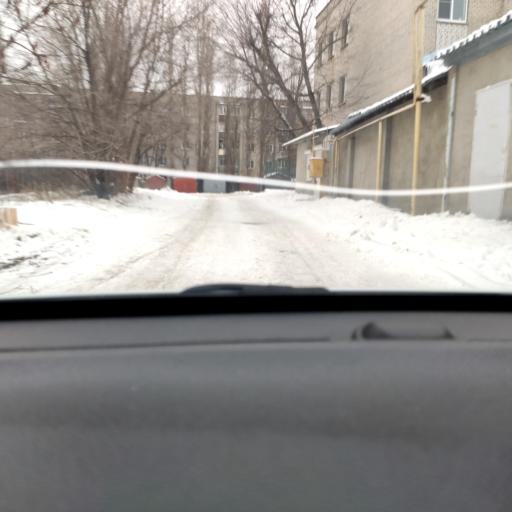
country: RU
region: Voronezj
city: Somovo
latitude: 51.7431
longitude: 39.3583
